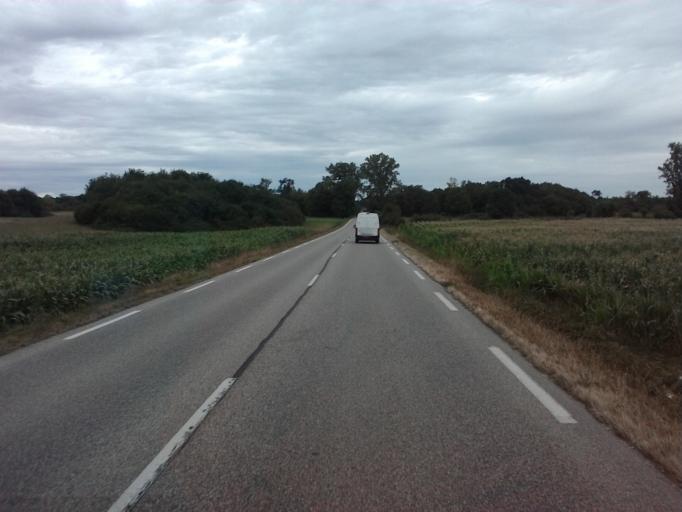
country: FR
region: Rhone-Alpes
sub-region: Departement de l'Isere
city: Sermerieu
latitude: 45.7210
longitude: 5.4159
